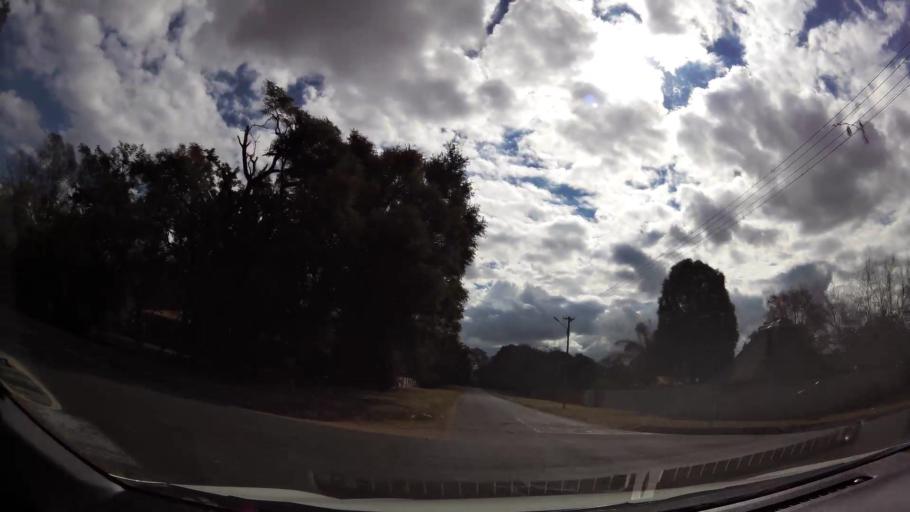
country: ZA
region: Limpopo
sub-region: Waterberg District Municipality
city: Modimolle
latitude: -24.7072
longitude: 28.4053
